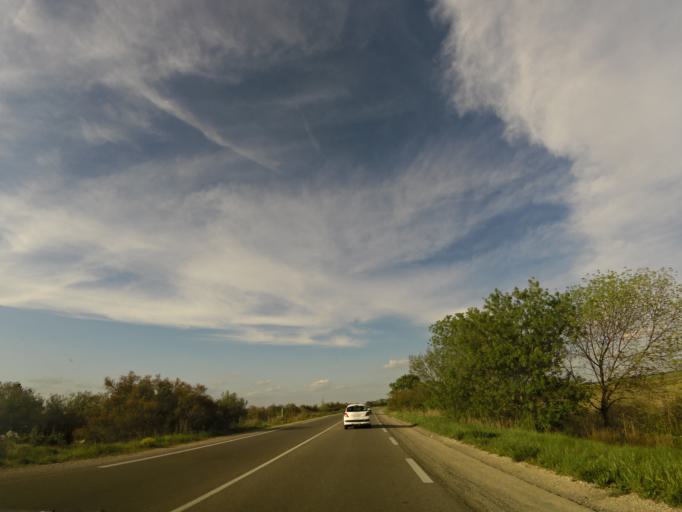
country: FR
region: Languedoc-Roussillon
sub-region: Departement de l'Herault
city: Saint-Just
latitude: 43.6151
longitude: 4.1125
